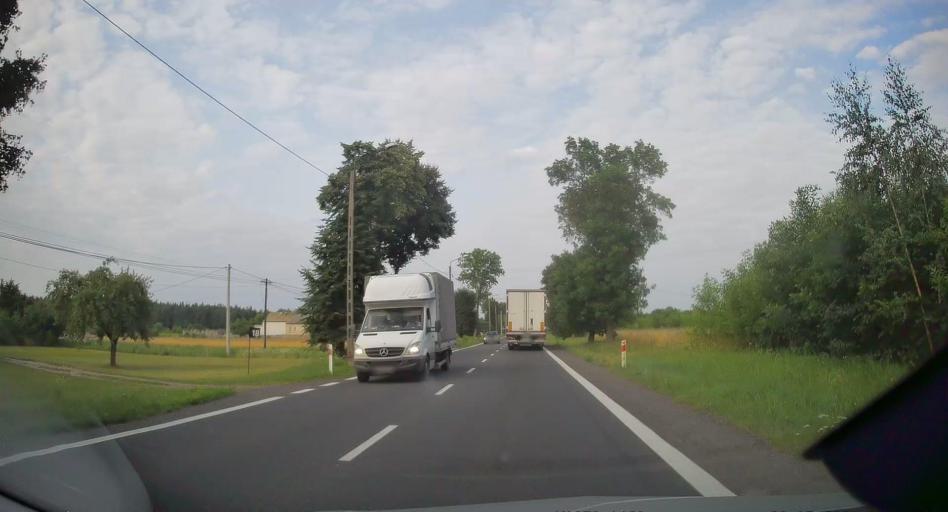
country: PL
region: Silesian Voivodeship
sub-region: Powiat czestochowski
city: Rudniki
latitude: 50.8916
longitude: 19.2700
